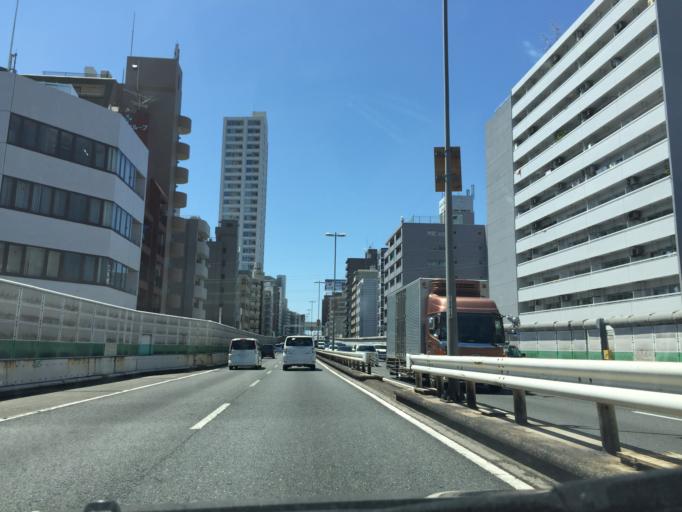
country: JP
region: Tokyo
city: Tokyo
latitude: 35.6401
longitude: 139.6683
